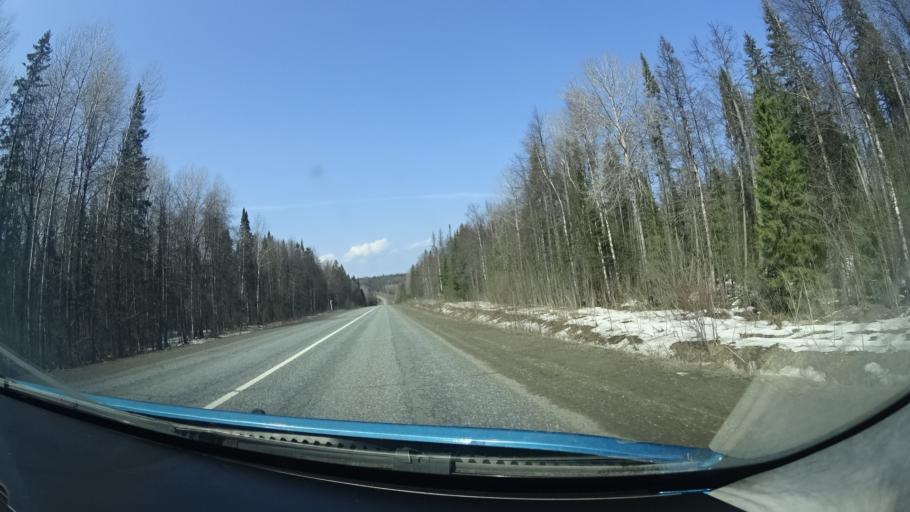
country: RU
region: Perm
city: Yugo-Kamskiy
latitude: 57.5862
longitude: 55.6729
